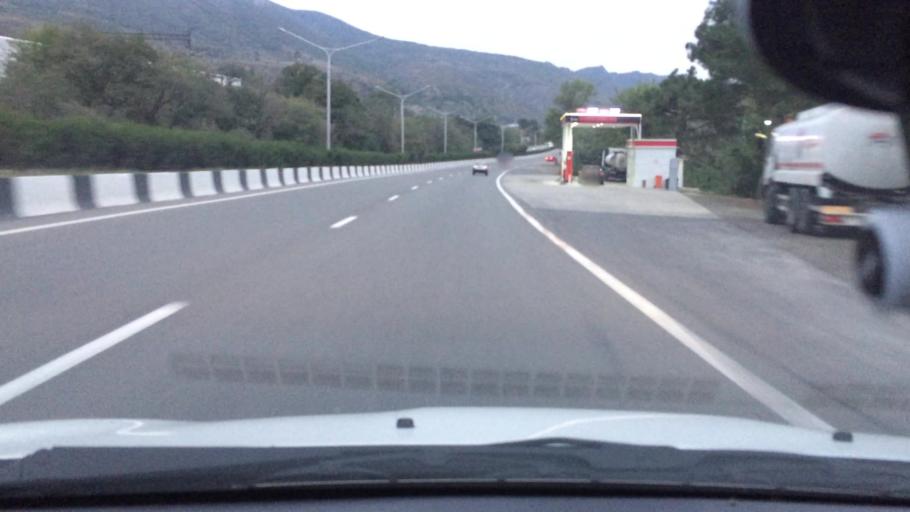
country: GE
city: Zahesi
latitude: 41.8186
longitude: 44.7467
